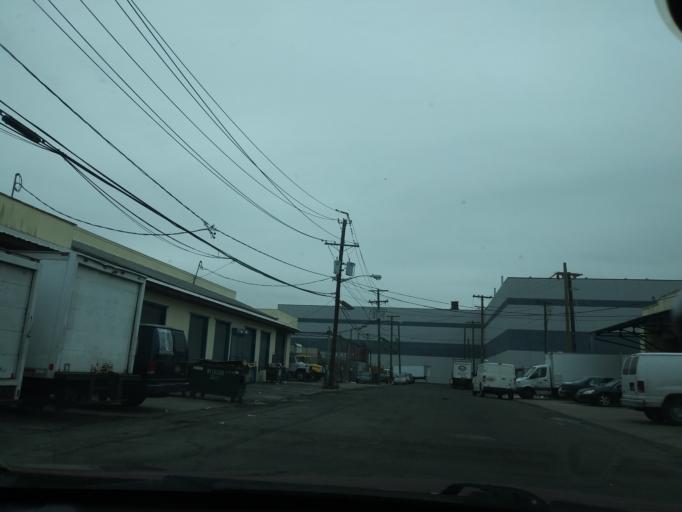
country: US
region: New Jersey
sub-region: Essex County
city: Newark
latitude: 40.7173
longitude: -74.1783
